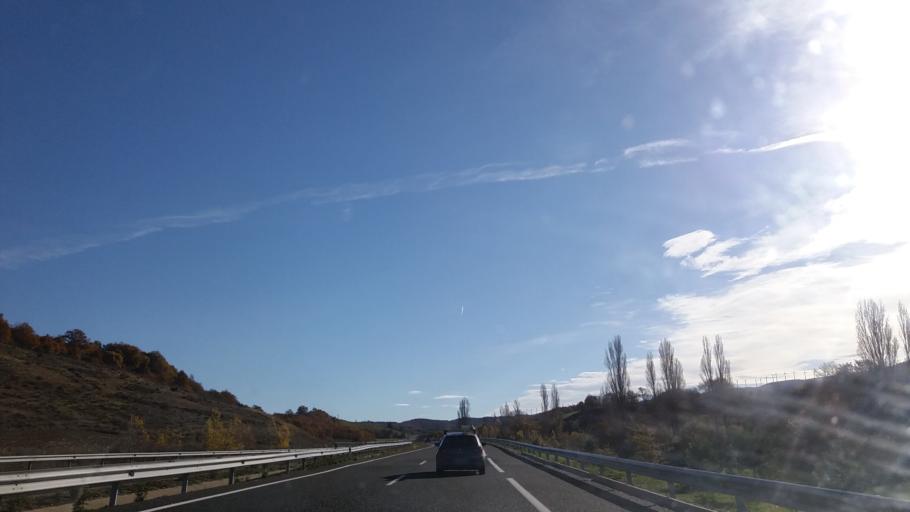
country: ES
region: Navarre
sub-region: Provincia de Navarra
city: Monreal
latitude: 42.6800
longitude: -1.4628
